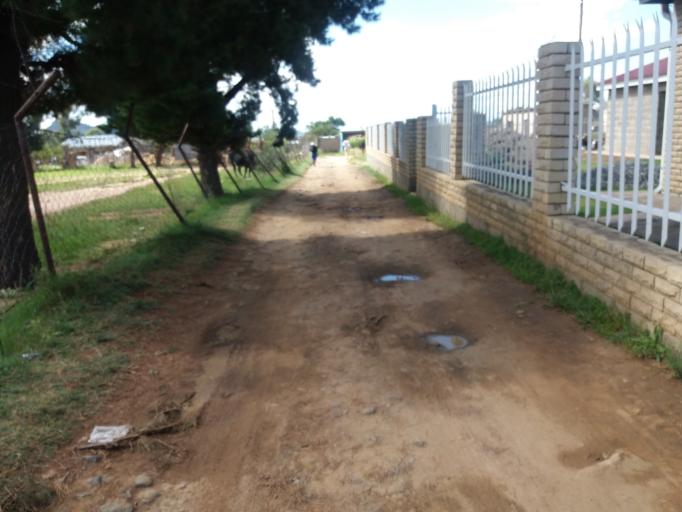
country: LS
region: Maseru
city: Maseru
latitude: -29.3714
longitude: 27.5096
